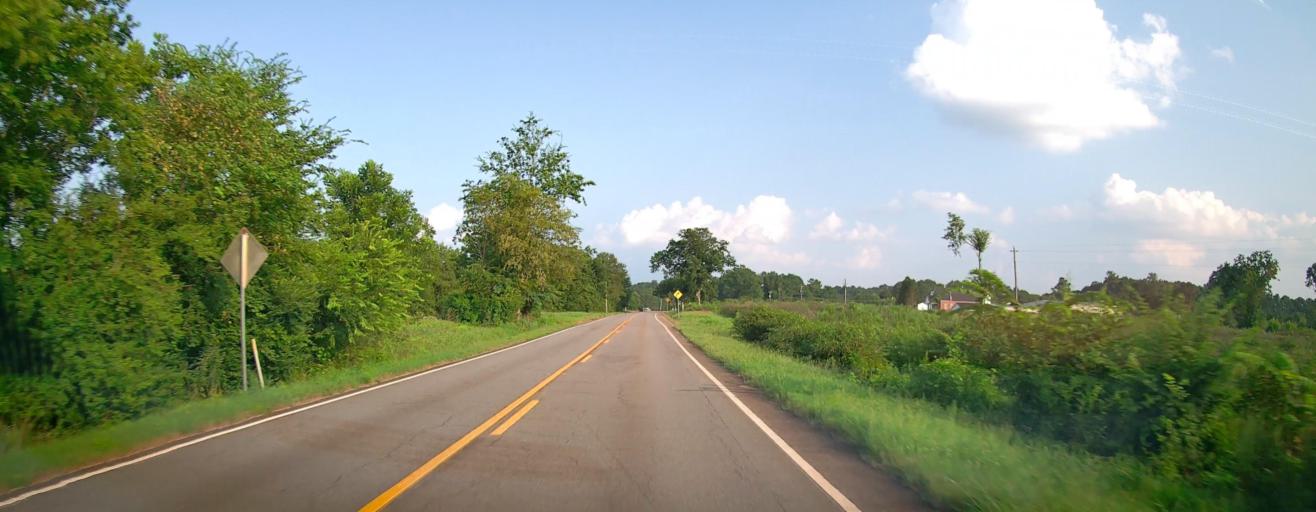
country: US
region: Georgia
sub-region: Jones County
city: Gray
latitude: 33.0569
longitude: -83.5610
